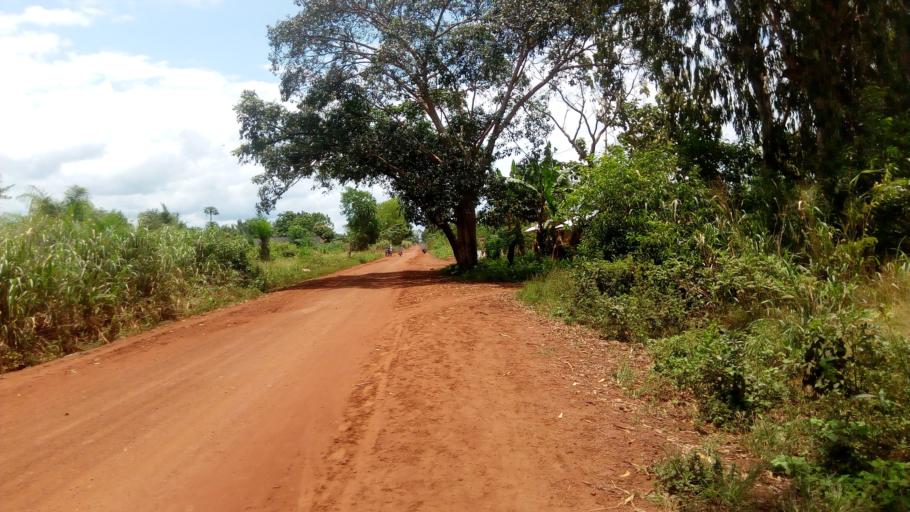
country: TG
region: Maritime
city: Tsevie
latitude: 6.3340
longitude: 1.0865
